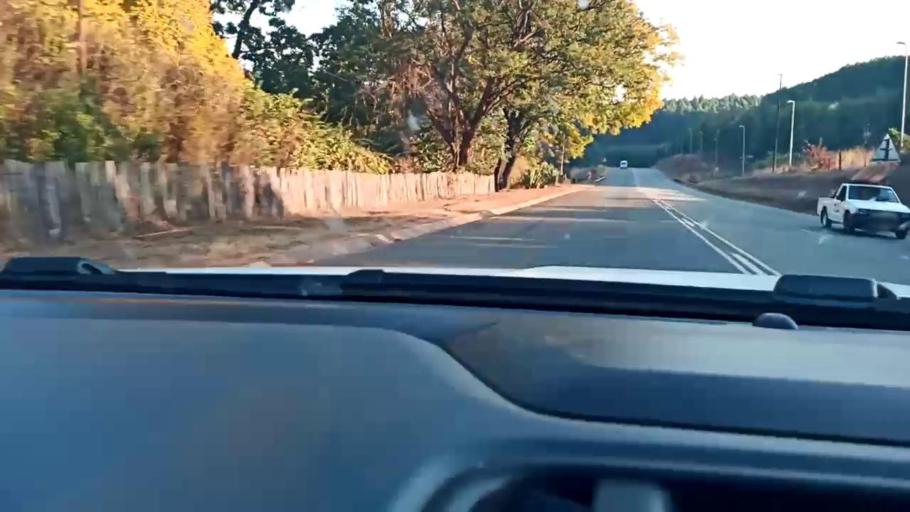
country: ZA
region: Limpopo
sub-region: Mopani District Municipality
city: Duiwelskloof
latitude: -23.7048
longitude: 30.1327
